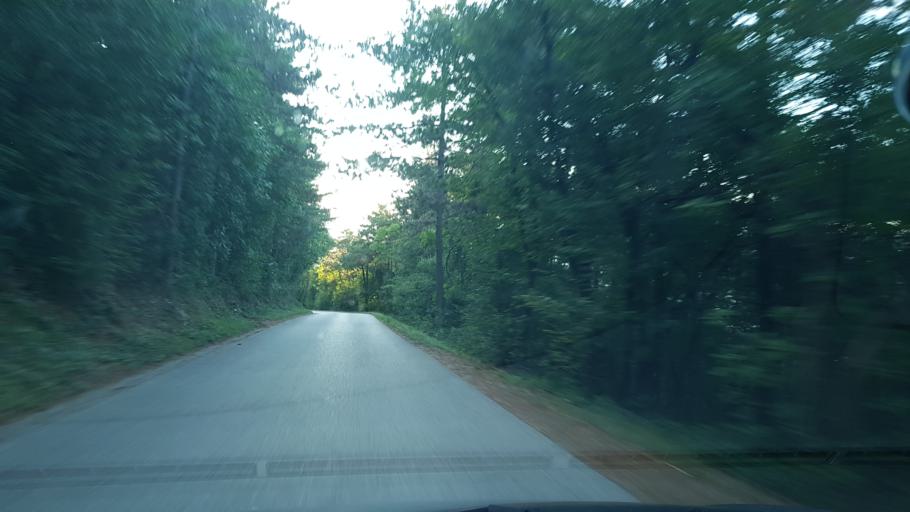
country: SI
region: Rence-Vogrsko
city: Rence
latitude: 45.8682
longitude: 13.6610
